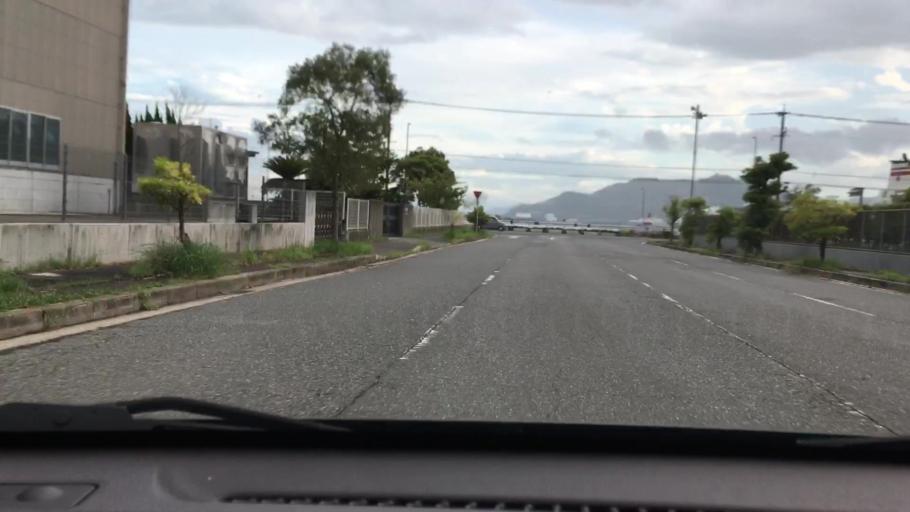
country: JP
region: Yamaguchi
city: Shimonoseki
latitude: 33.8871
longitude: 130.9928
